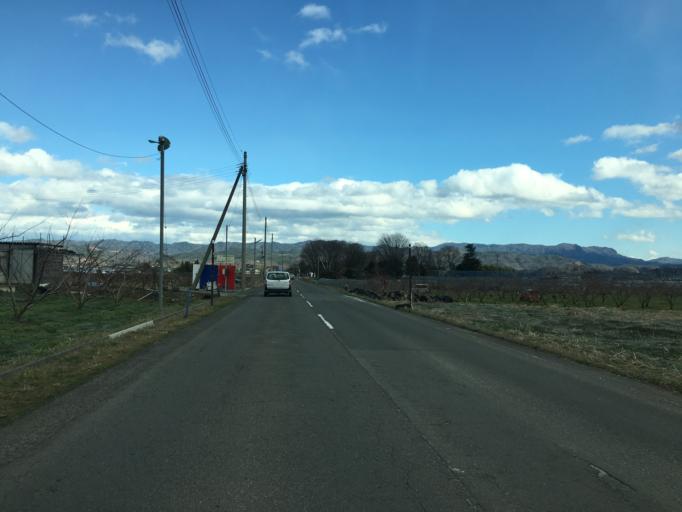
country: JP
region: Fukushima
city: Yanagawamachi-saiwaicho
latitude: 37.8585
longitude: 140.5748
